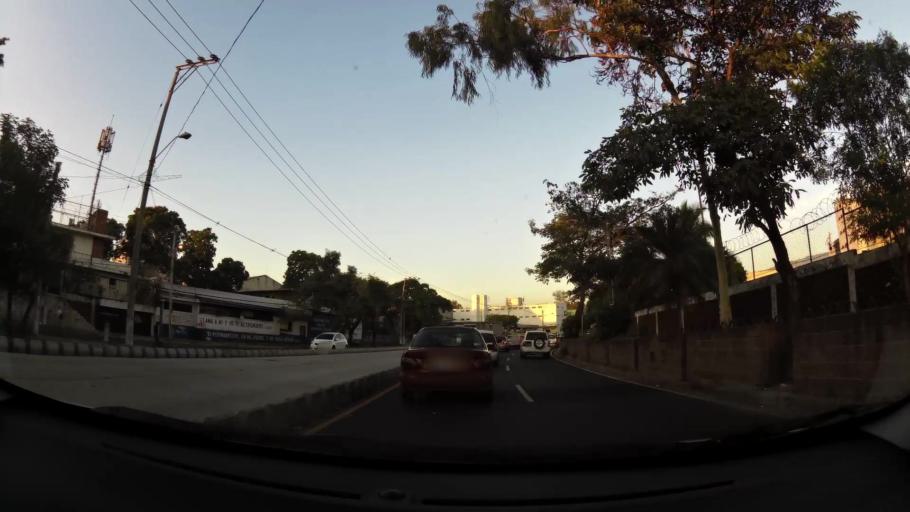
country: SV
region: San Salvador
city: San Salvador
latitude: 13.7026
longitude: -89.2028
